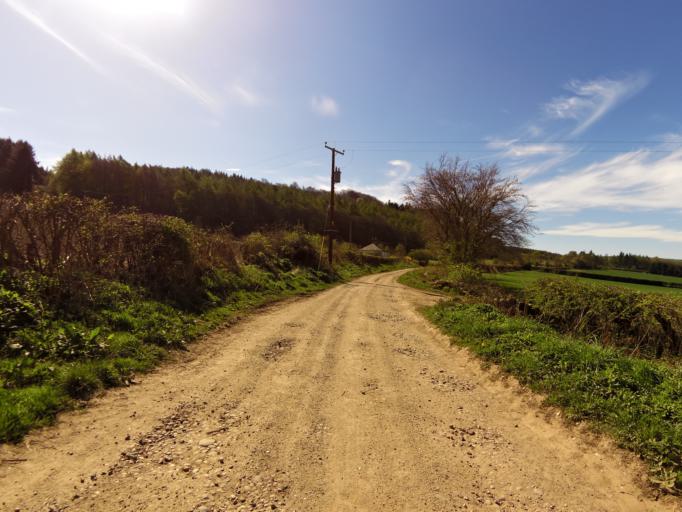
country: GB
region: Scotland
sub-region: Fife
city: Cupar
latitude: 56.3985
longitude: -3.0652
